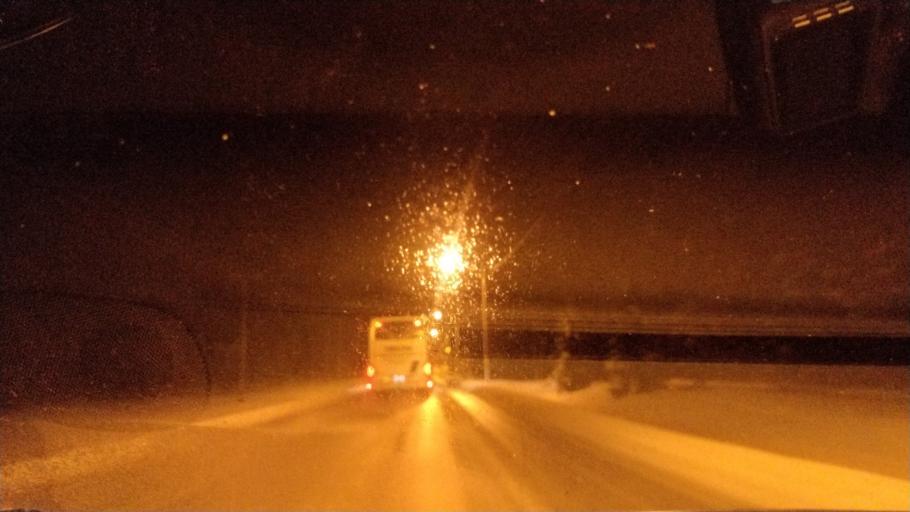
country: FI
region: Lapland
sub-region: Rovaniemi
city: Rovaniemi
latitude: 66.2943
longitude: 25.3510
